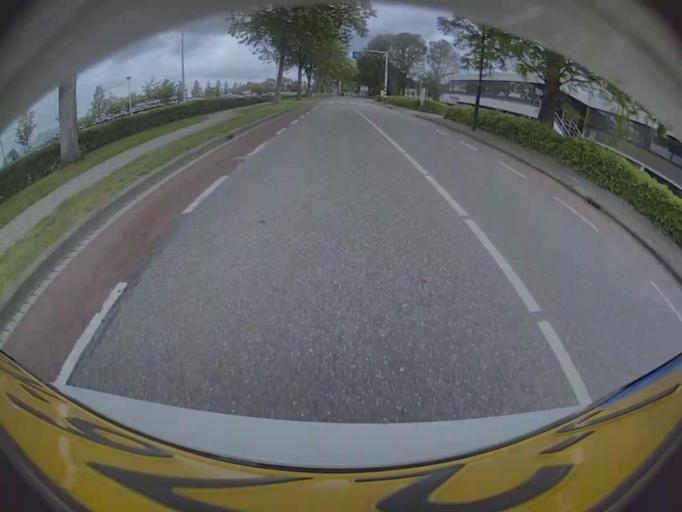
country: NL
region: South Holland
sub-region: Gemeente Voorschoten
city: Voorschoten
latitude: 52.1253
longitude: 4.4341
